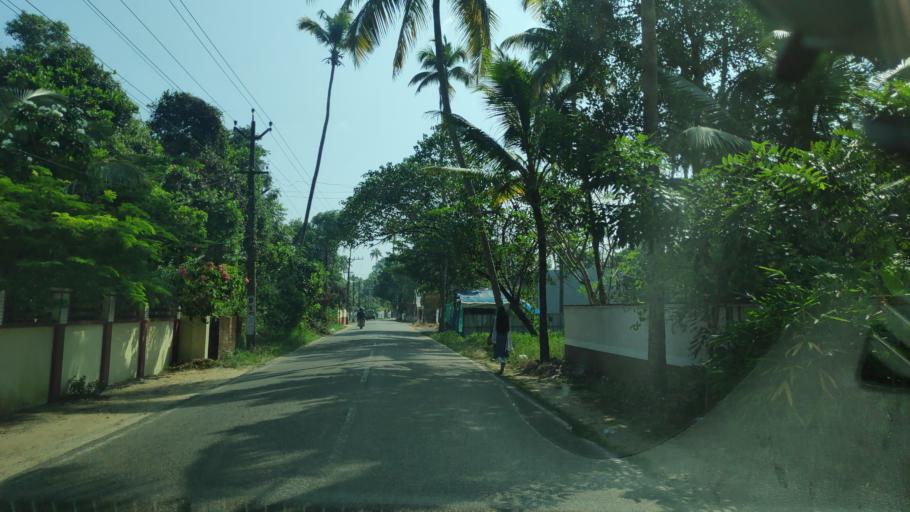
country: IN
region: Kerala
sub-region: Alappuzha
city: Vayalar
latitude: 9.6509
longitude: 76.2998
